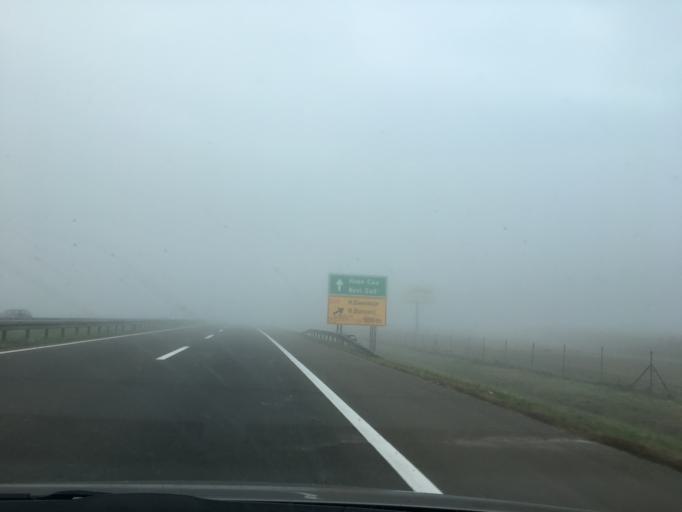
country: RS
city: Novi Banovci
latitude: 44.9390
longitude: 20.2895
